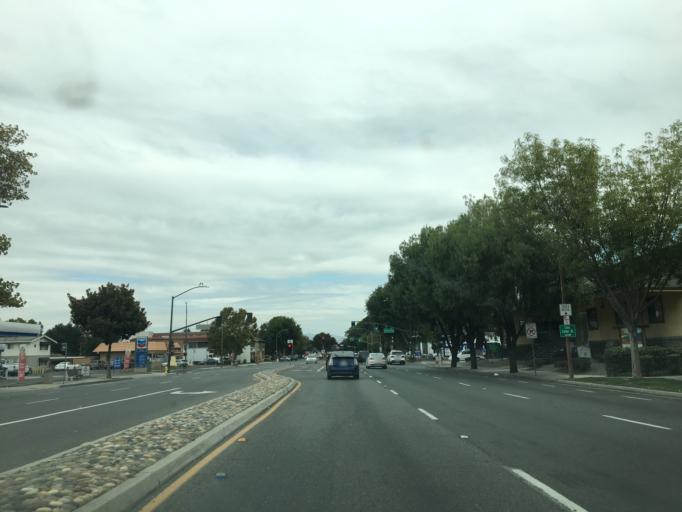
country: US
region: California
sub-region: Santa Clara County
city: Campbell
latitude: 37.2942
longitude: -121.9447
